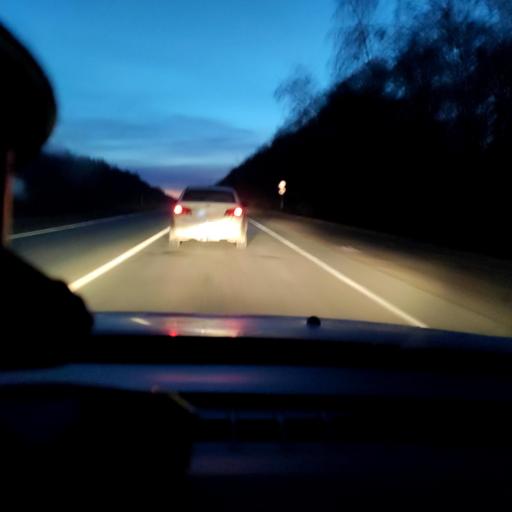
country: RU
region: Samara
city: Novokuybyshevsk
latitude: 52.9830
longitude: 49.8825
